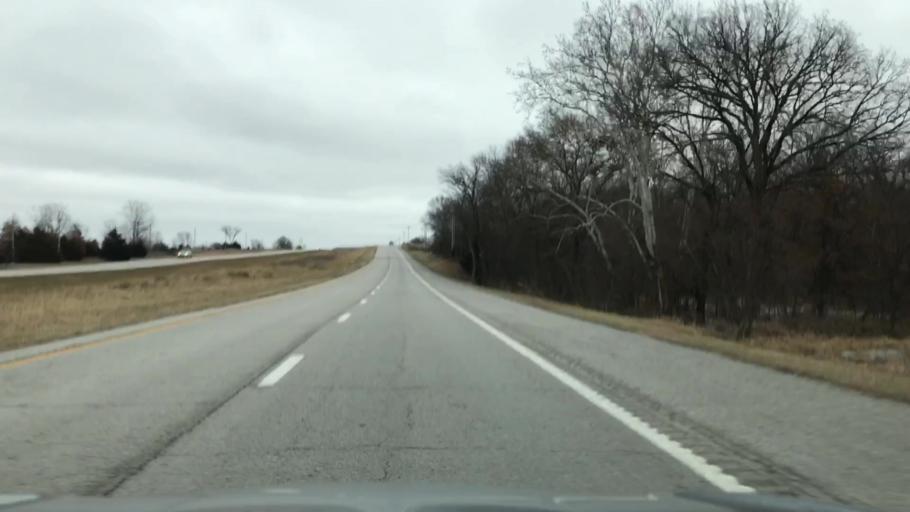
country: US
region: Missouri
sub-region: Linn County
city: Linneus
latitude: 39.7780
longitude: -93.2063
